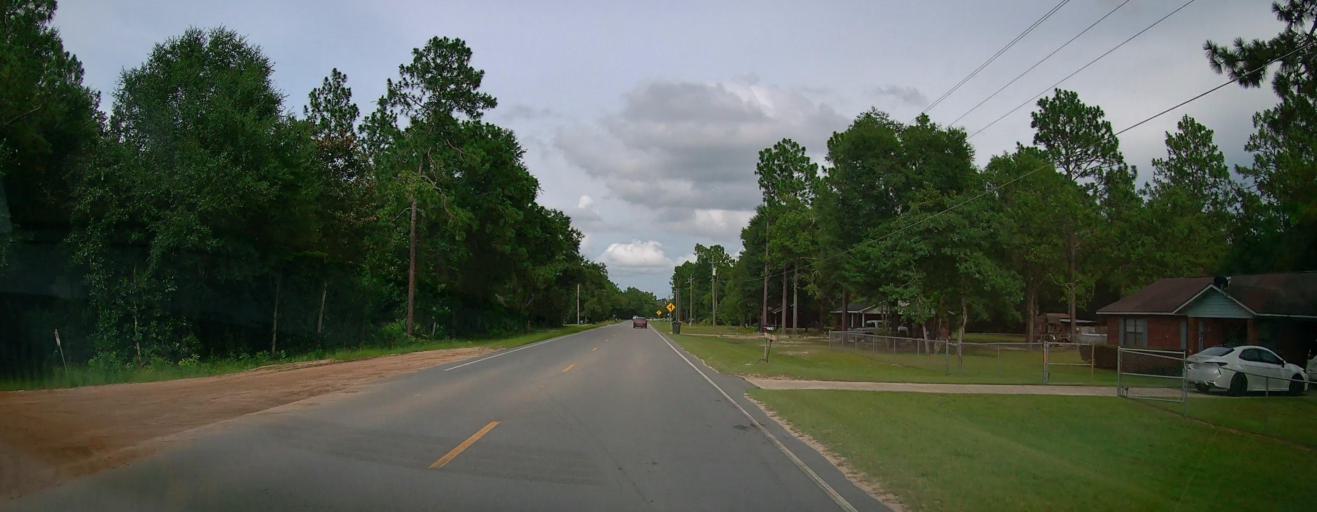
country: US
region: Georgia
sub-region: Wayne County
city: Jesup
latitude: 31.6571
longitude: -81.9017
